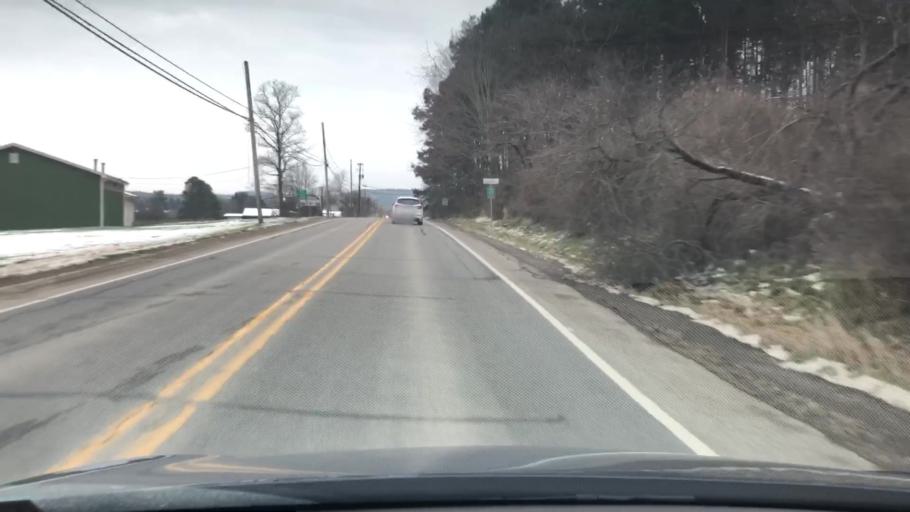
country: US
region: Pennsylvania
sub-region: Jefferson County
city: Brookville
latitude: 41.1241
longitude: -79.1834
